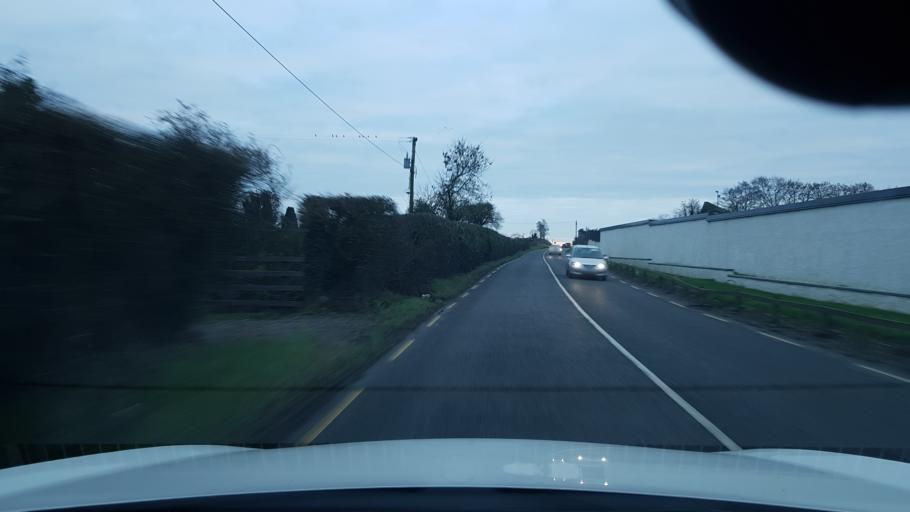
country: IE
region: Leinster
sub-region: An Mhi
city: Navan
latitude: 53.6846
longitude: -6.6730
